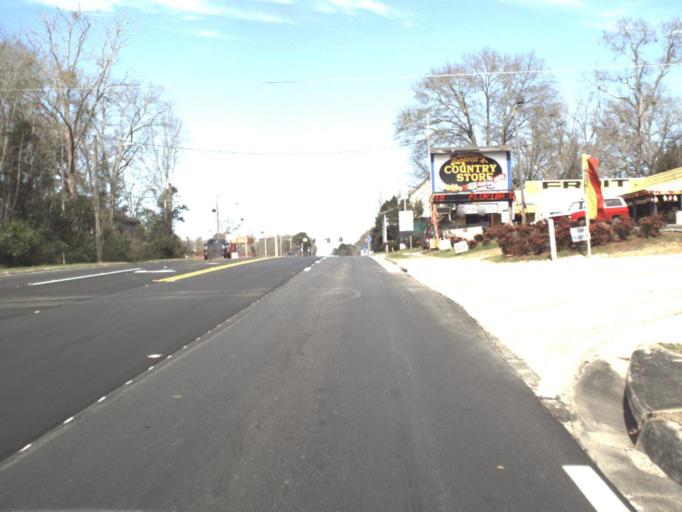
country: US
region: Florida
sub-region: Washington County
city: Chipley
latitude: 30.6918
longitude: -85.3922
